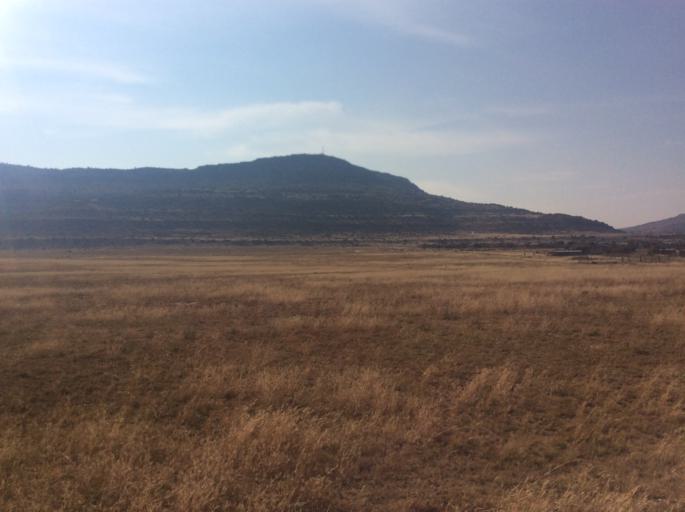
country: LS
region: Mafeteng
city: Mafeteng
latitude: -29.7089
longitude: 27.0088
